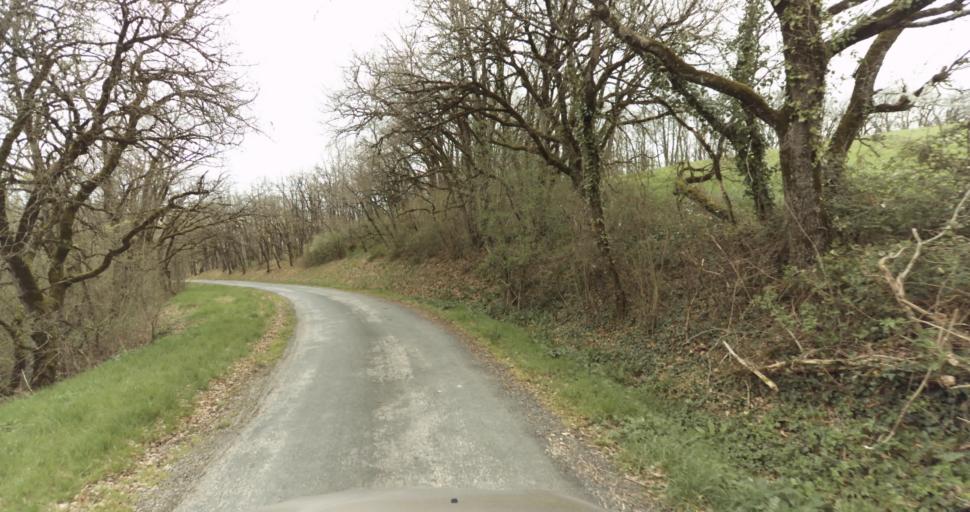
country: FR
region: Midi-Pyrenees
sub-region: Departement du Tarn
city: Puygouzon
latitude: 43.8658
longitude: 2.1814
